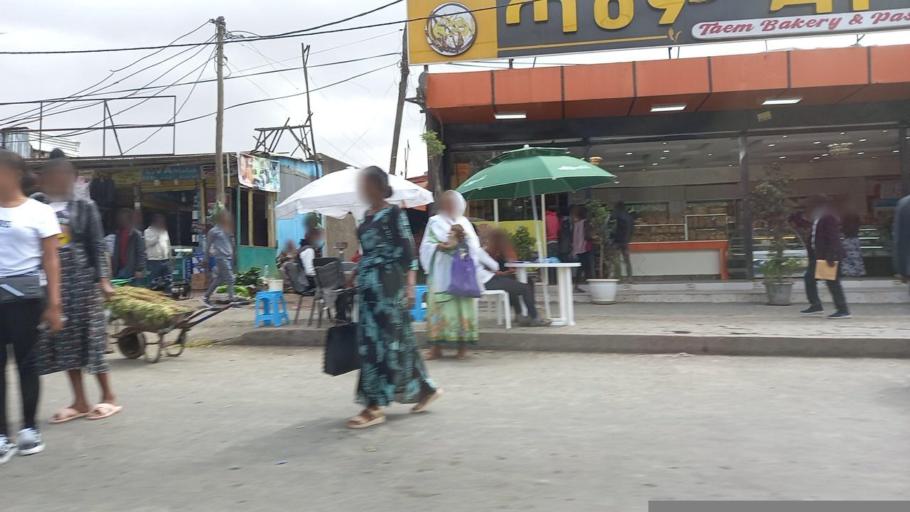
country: ET
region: Adis Abeba
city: Addis Ababa
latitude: 9.0204
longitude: 38.8601
